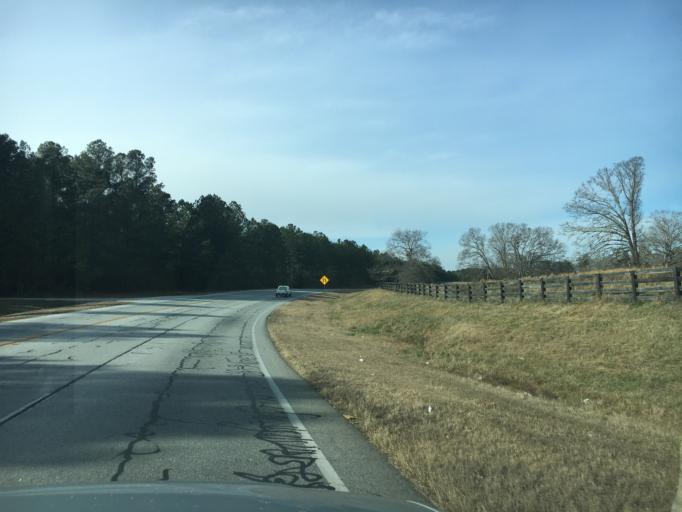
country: US
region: Georgia
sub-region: Jackson County
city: Hoschton
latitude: 34.0730
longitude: -83.7363
